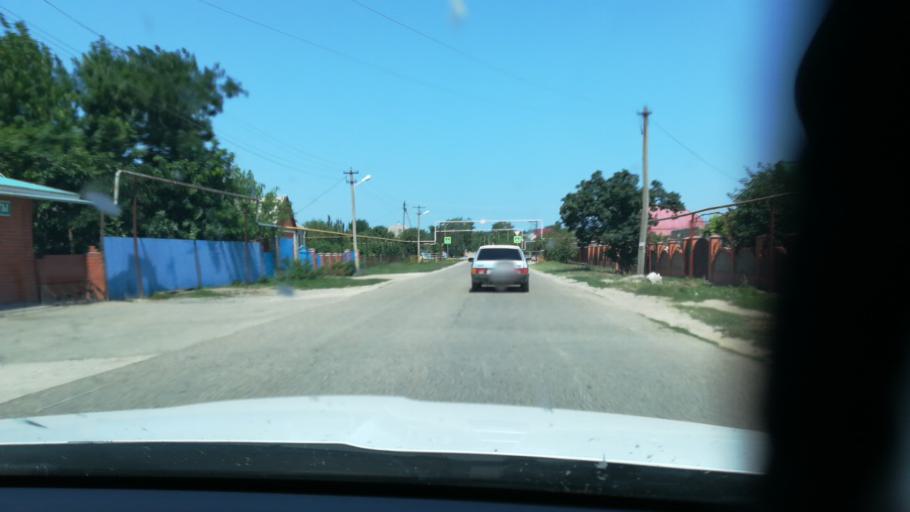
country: RU
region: Krasnodarskiy
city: Starotitarovskaya
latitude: 45.2158
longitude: 37.1425
